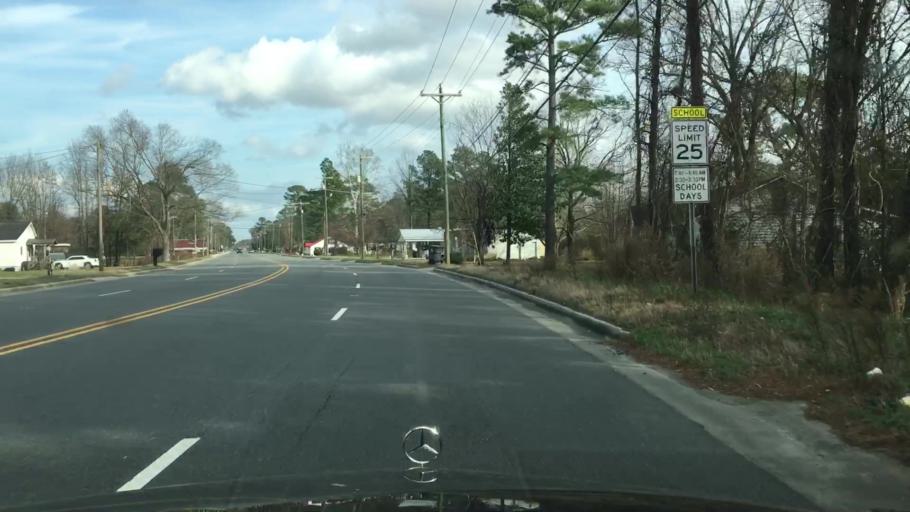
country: US
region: North Carolina
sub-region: Duplin County
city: Warsaw
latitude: 34.9943
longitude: -78.1114
